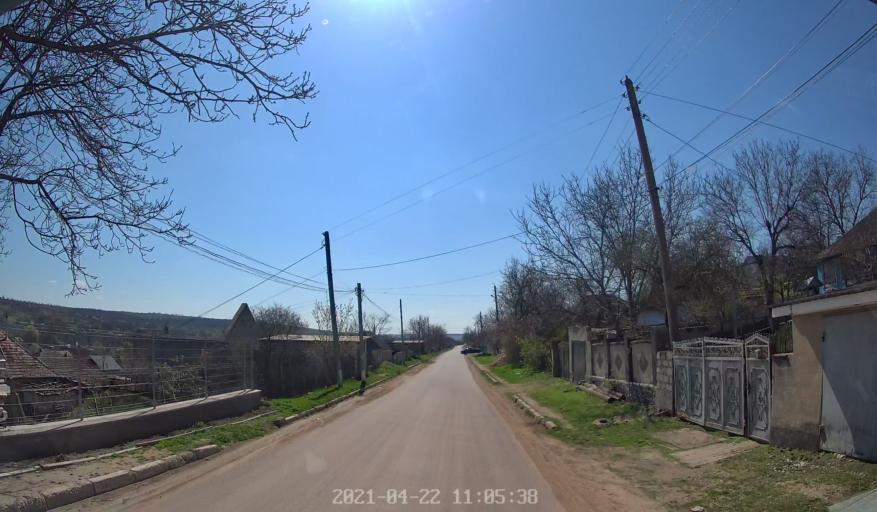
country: MD
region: Chisinau
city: Ciorescu
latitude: 47.1651
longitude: 28.9495
